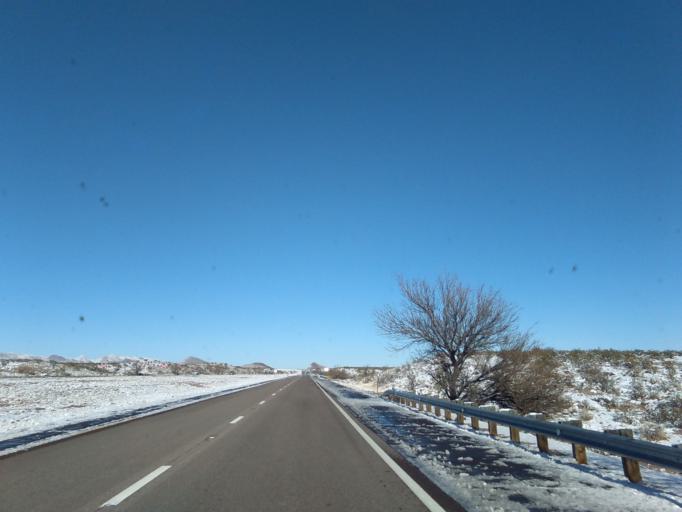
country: US
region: New Mexico
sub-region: Socorro County
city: Socorro
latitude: 33.7248
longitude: -107.0244
